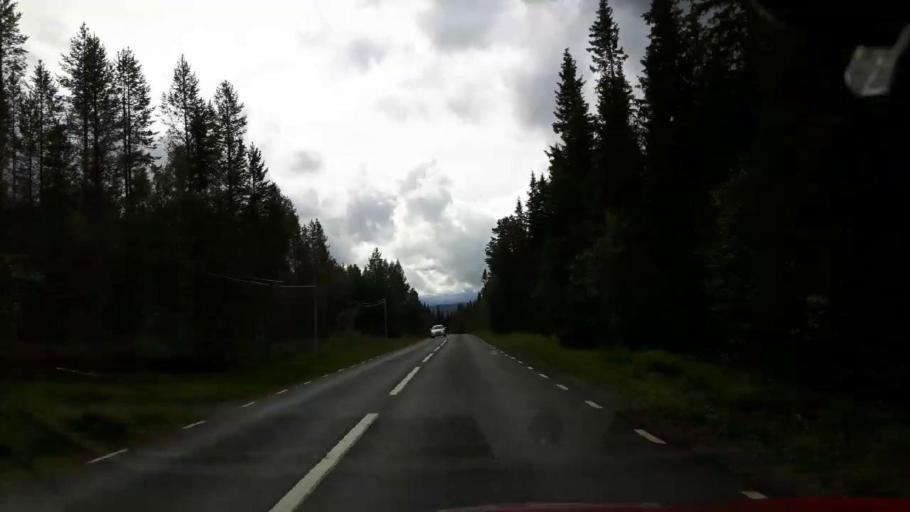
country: NO
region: Nord-Trondelag
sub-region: Lierne
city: Sandvika
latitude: 64.5151
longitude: 14.1585
